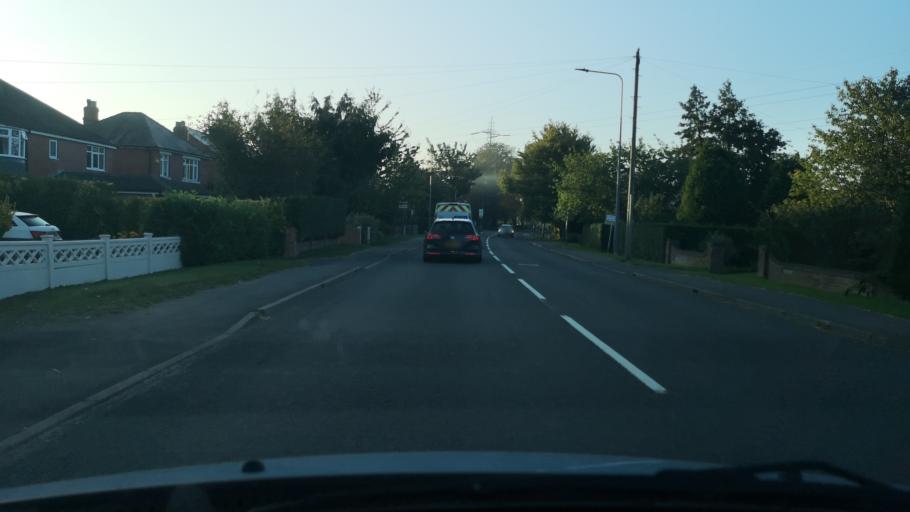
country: GB
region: England
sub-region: North Lincolnshire
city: Crowle
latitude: 53.6018
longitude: -0.8289
